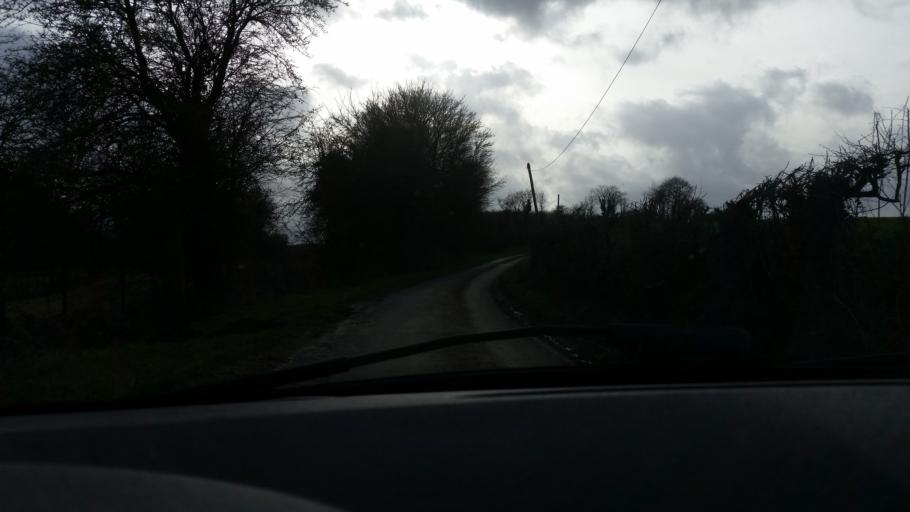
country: FR
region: Nord-Pas-de-Calais
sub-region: Departement du Nord
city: Jeumont
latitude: 50.2446
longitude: 4.1059
